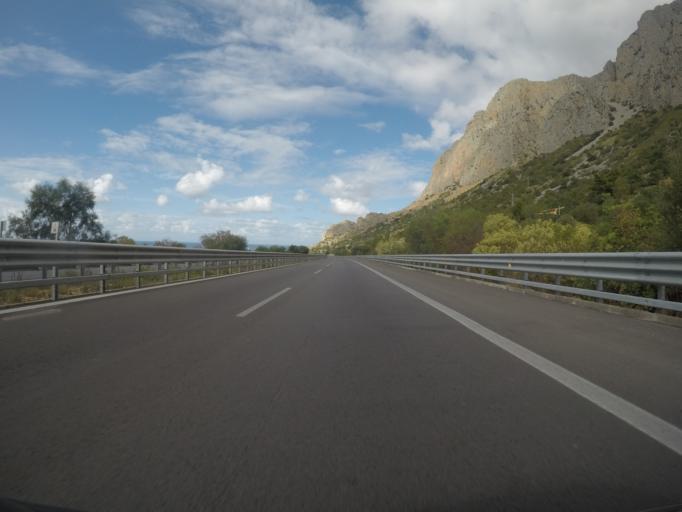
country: IT
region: Sicily
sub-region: Palermo
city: Cinisi
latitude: 38.1582
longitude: 13.1141
